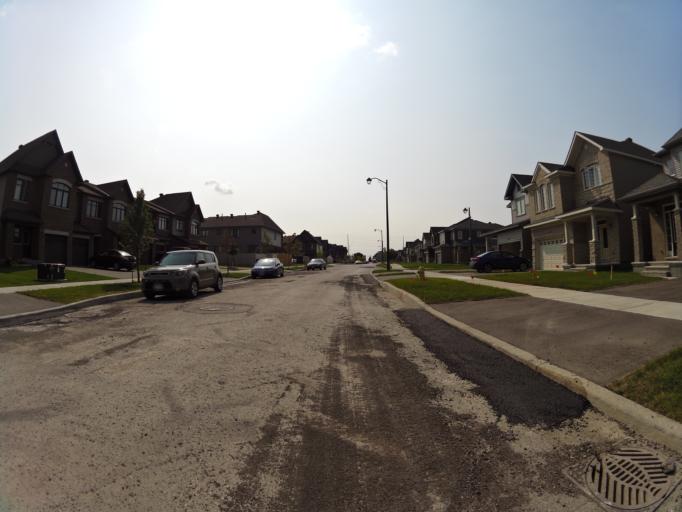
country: CA
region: Ontario
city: Bells Corners
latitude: 45.3055
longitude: -75.9371
